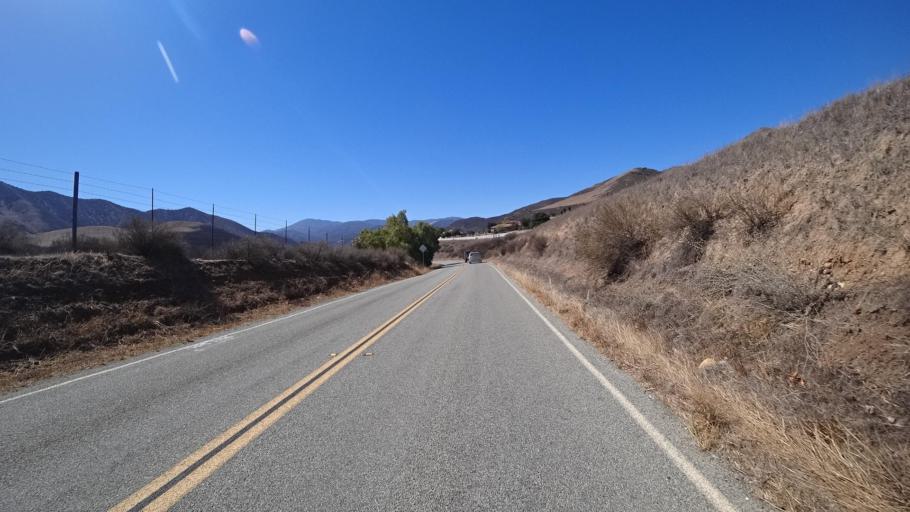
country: US
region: California
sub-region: Monterey County
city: Greenfield
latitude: 36.2847
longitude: -121.3179
